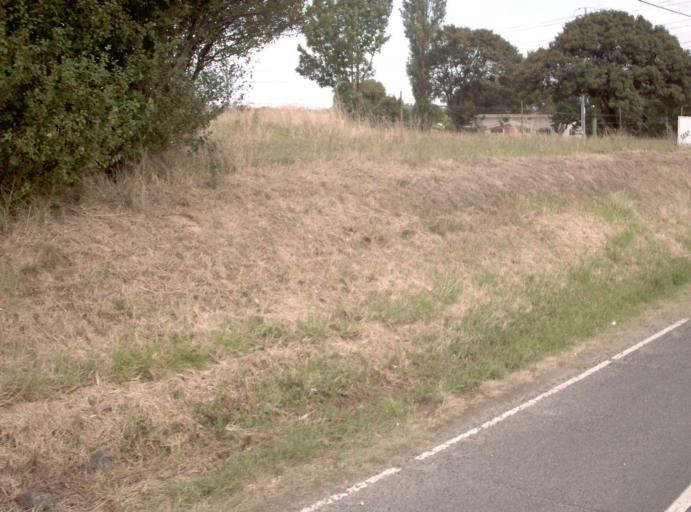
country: AU
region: Victoria
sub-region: Knox
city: Rowville
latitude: -37.9409
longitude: 145.2307
